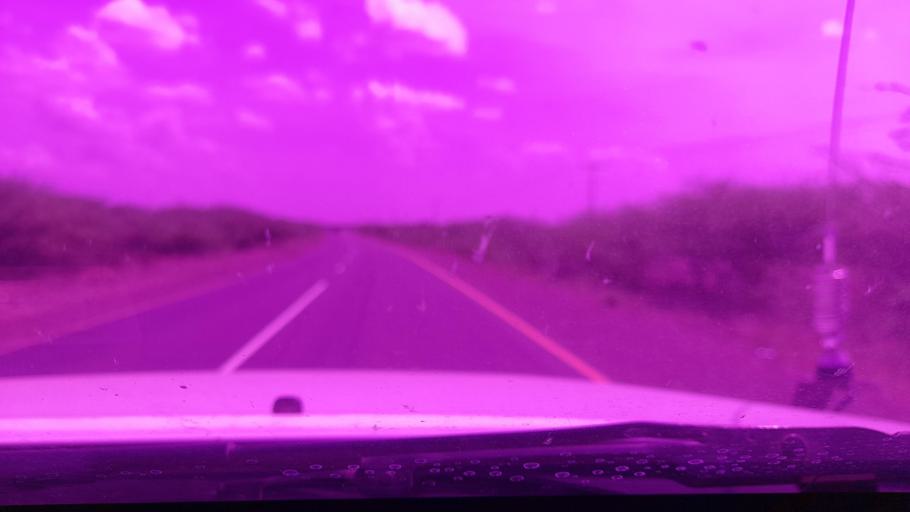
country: ET
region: Afar
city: Awash
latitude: 9.3576
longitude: 40.3049
